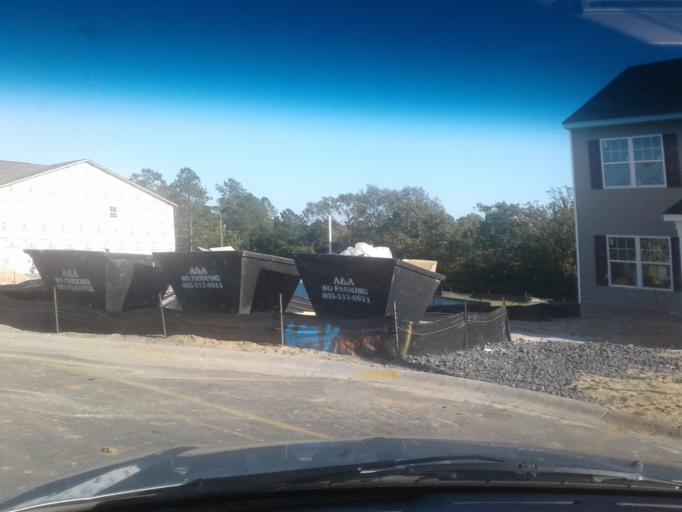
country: US
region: South Carolina
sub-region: Richland County
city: Woodfield
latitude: 34.0762
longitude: -80.8906
